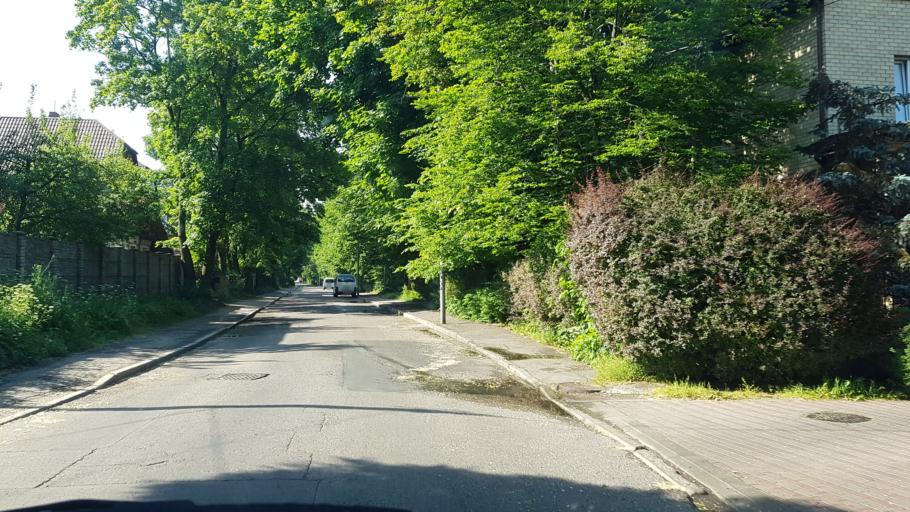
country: RU
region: Kaliningrad
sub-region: Gorod Kaliningrad
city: Kaliningrad
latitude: 54.7174
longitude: 20.4570
